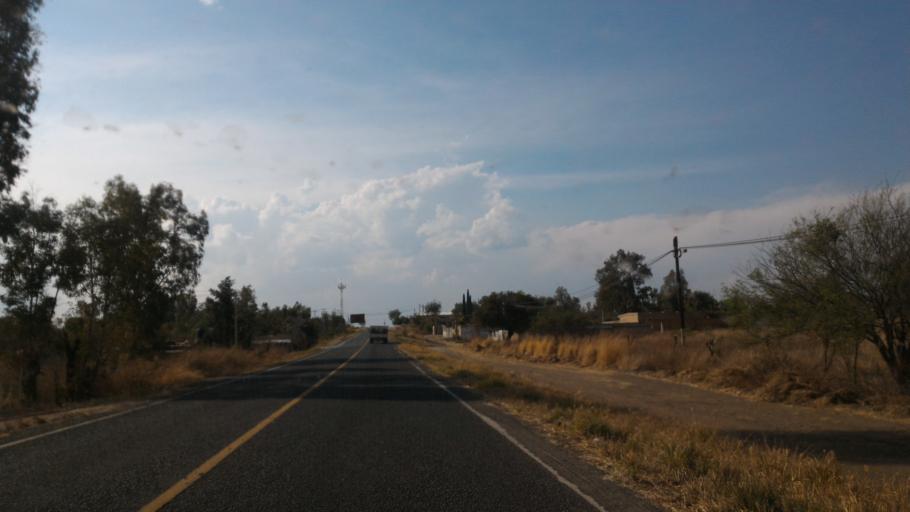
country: MX
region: Guanajuato
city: Ciudad Manuel Doblado
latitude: 20.8008
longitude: -101.9899
